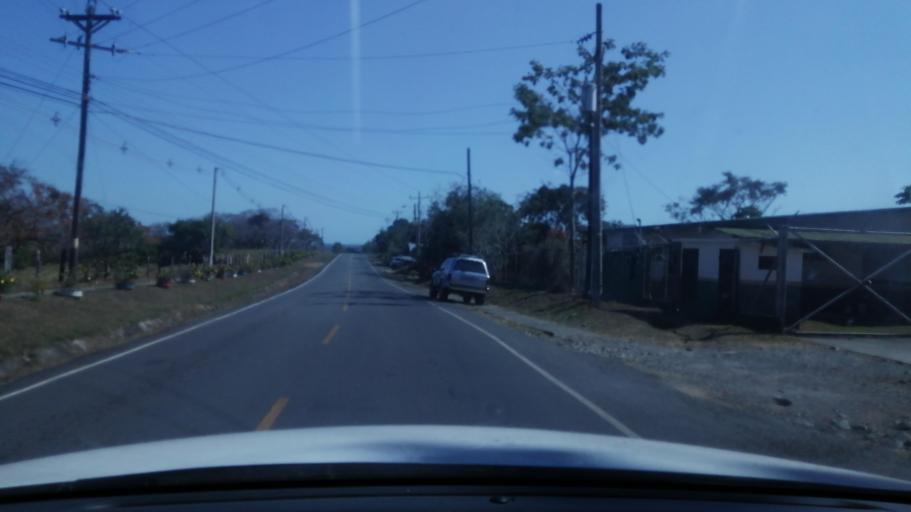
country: PA
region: Chiriqui
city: San Felix
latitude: 8.2846
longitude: -81.8738
